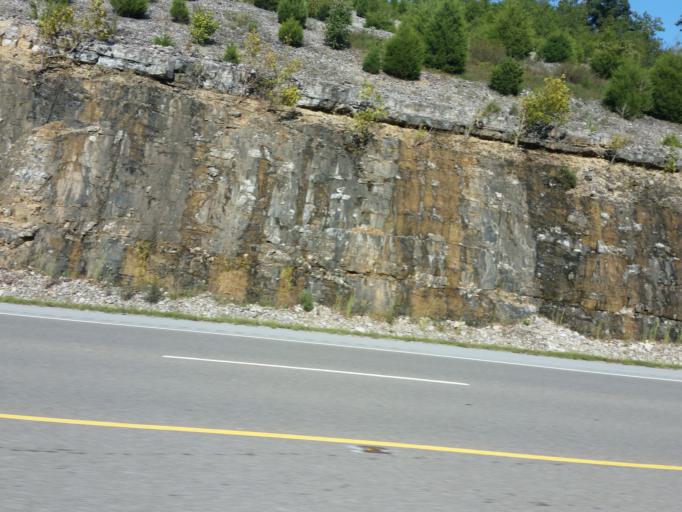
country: US
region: Tennessee
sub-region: Claiborne County
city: New Tazewell
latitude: 36.5156
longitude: -83.6111
